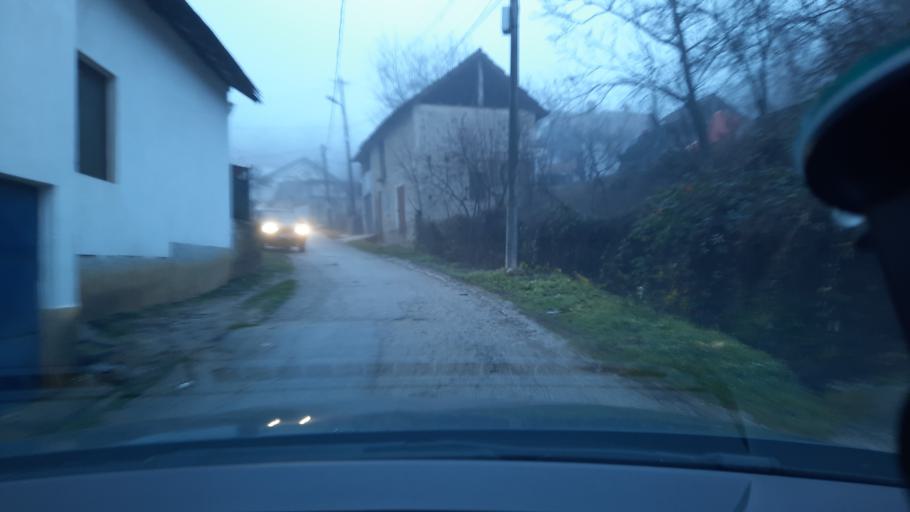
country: MK
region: Vrapciste
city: Vrapciste
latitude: 41.8409
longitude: 20.8786
